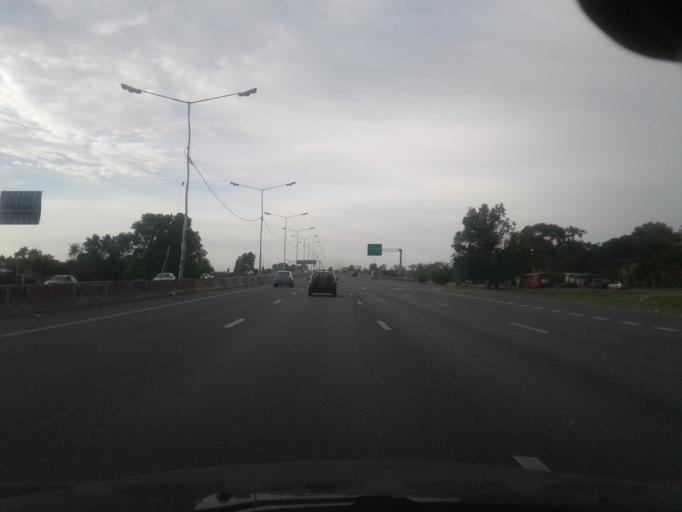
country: AR
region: Santa Fe
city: Perez
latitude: -32.9358
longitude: -60.7229
